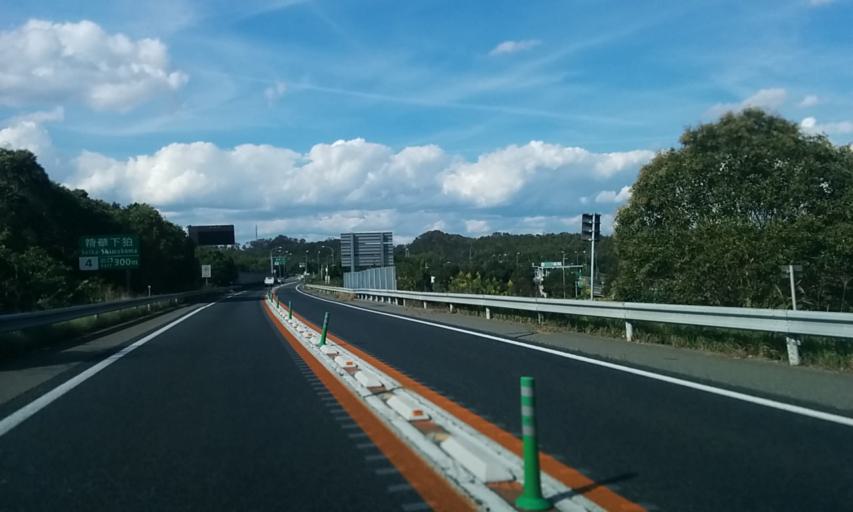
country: JP
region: Kyoto
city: Tanabe
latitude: 34.7722
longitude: 135.7742
